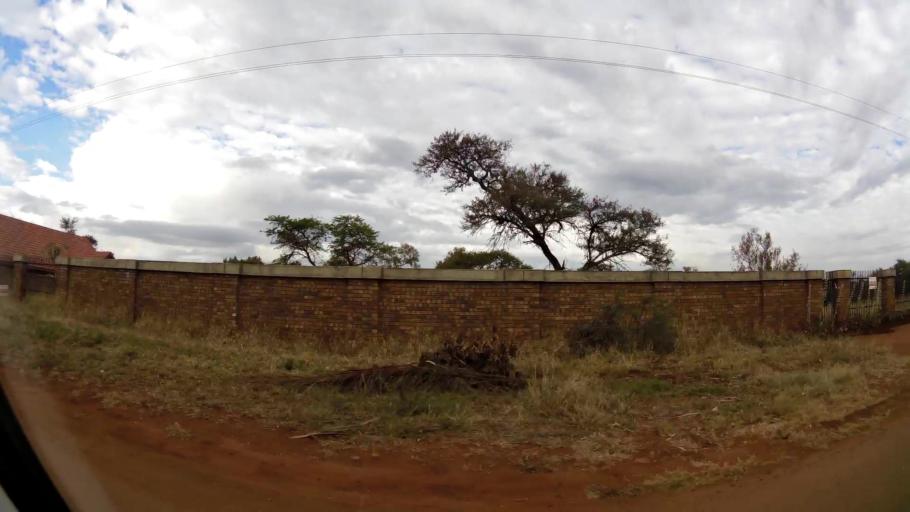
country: ZA
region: Limpopo
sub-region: Waterberg District Municipality
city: Modimolle
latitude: -24.5068
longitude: 28.7191
